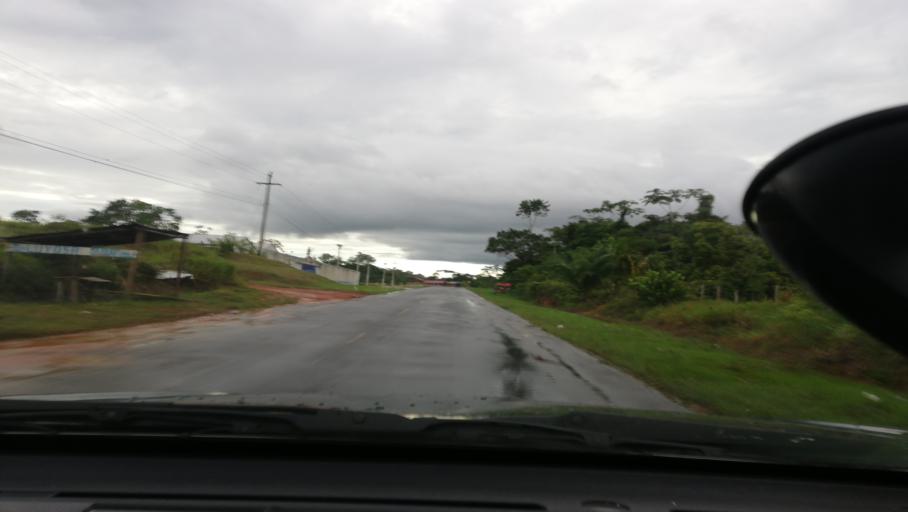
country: PE
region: Loreto
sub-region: Provincia de Maynas
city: Iquitos
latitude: -3.9137
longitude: -73.3641
